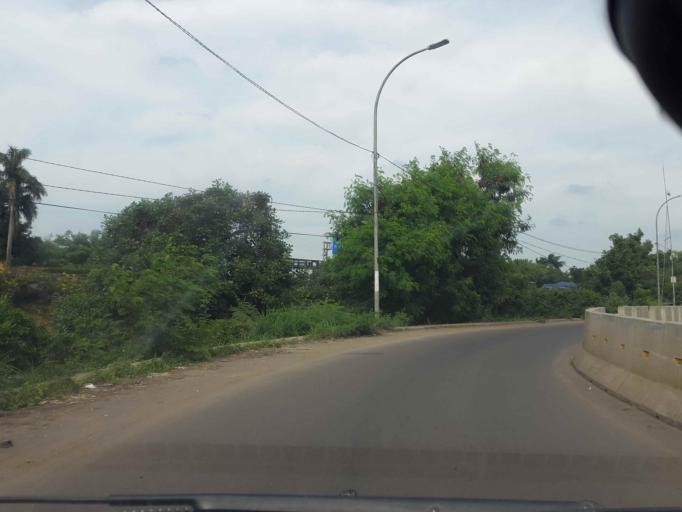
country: ID
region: Banten
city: Tangerang
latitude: -6.2211
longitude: 106.6485
